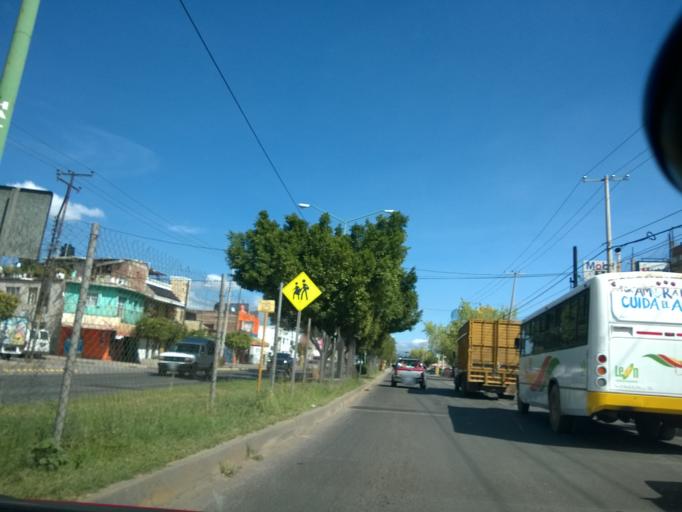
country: MX
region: Guanajuato
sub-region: Leon
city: San Jose de Duran (Los Troncoso)
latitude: 21.0934
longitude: -101.6793
